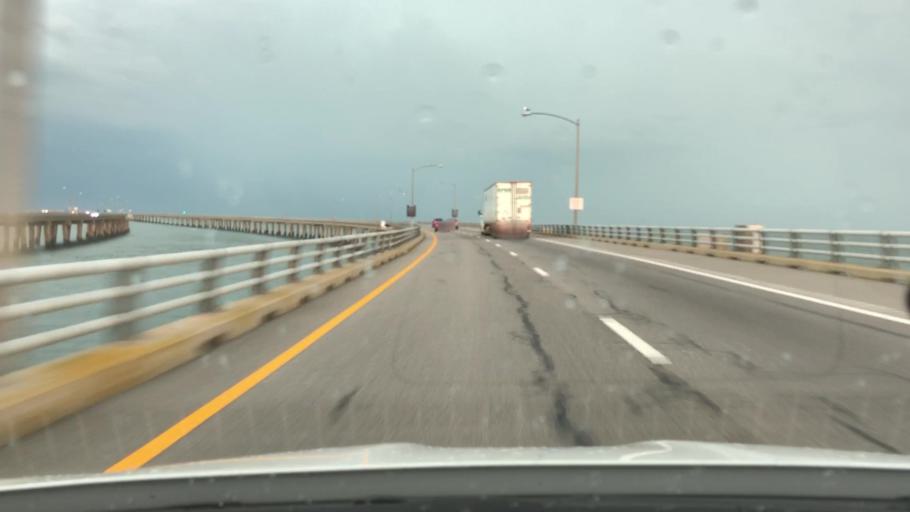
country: US
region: Virginia
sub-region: City of Virginia Beach
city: Virginia Beach
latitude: 37.0317
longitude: -76.0849
